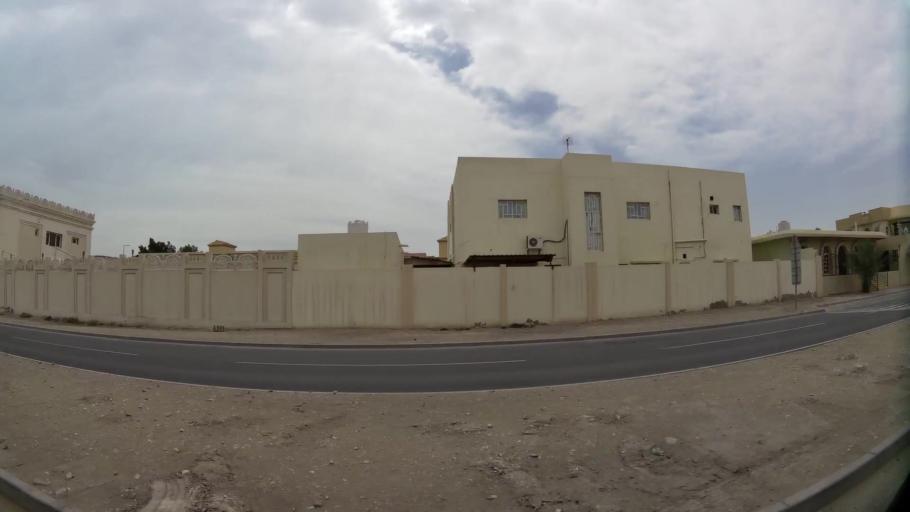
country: QA
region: Baladiyat ar Rayyan
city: Ar Rayyan
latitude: 25.2259
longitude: 51.4582
